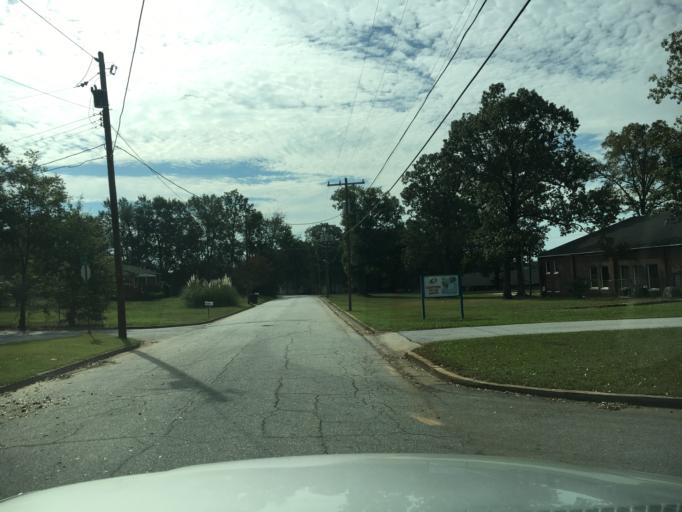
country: US
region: South Carolina
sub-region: Greenville County
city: Greer
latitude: 34.9296
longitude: -82.2243
